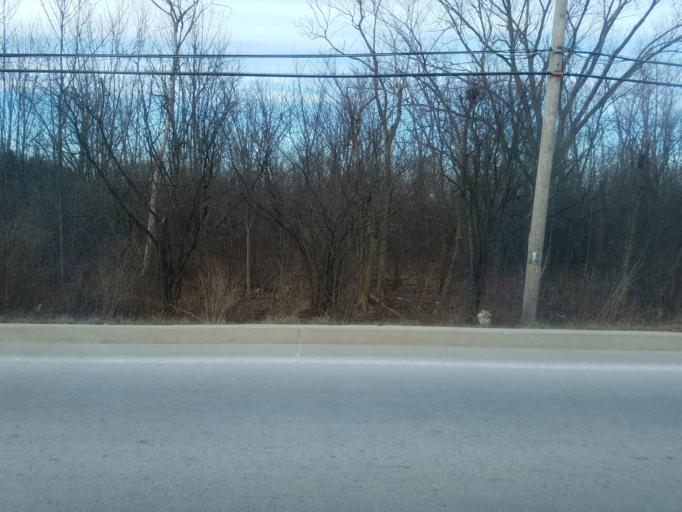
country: US
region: Illinois
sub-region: Cook County
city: Lemont
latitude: 41.6275
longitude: -88.0052
